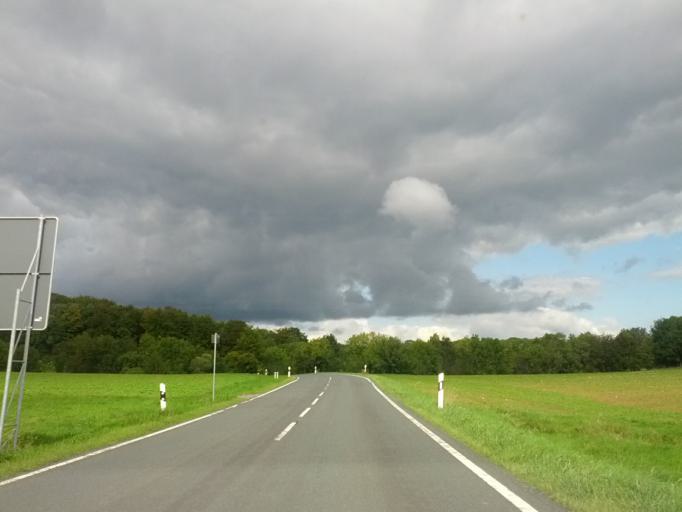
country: DE
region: Hesse
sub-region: Regierungsbezirk Kassel
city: Herleshausen
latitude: 51.0451
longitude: 10.1331
